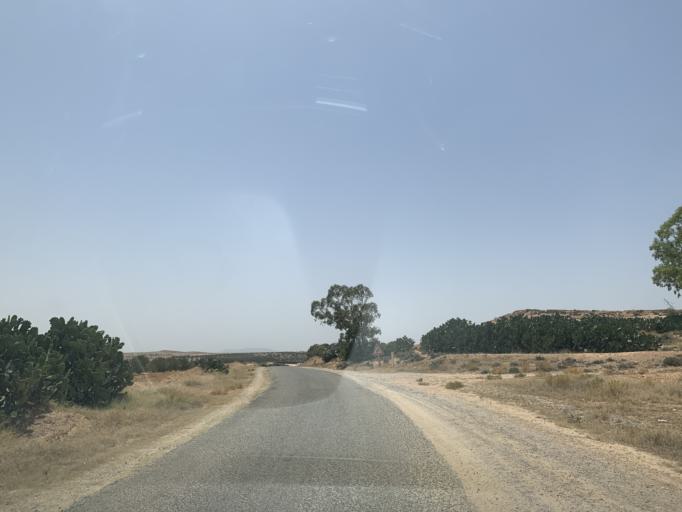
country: TN
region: Al Mahdiyah
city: Shurban
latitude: 35.1611
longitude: 10.2570
